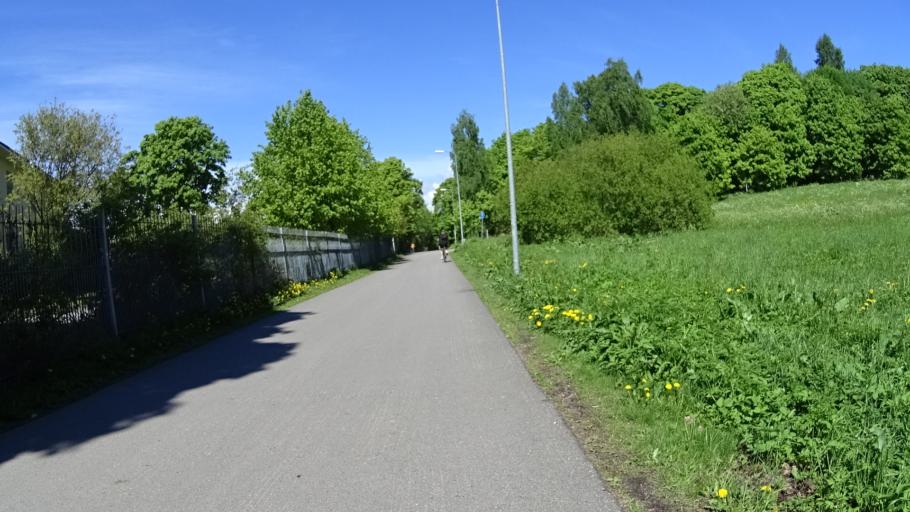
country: FI
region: Uusimaa
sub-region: Helsinki
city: Helsinki
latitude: 60.2024
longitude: 24.9585
